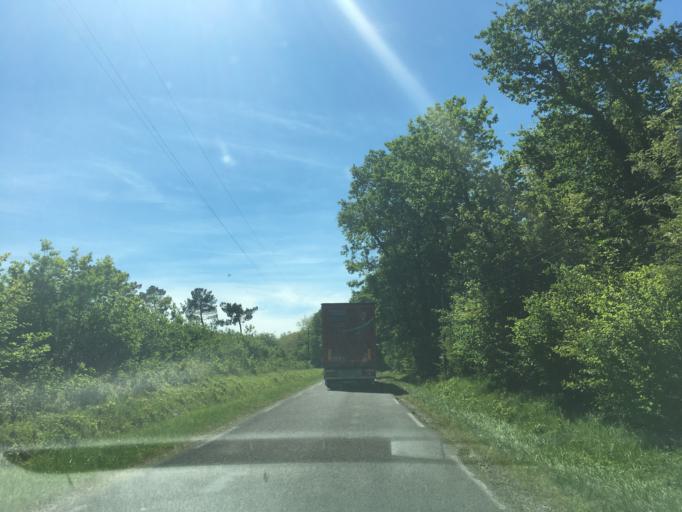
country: FR
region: Aquitaine
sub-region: Departement de la Gironde
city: Lesparre-Medoc
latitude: 45.2653
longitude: -0.8998
